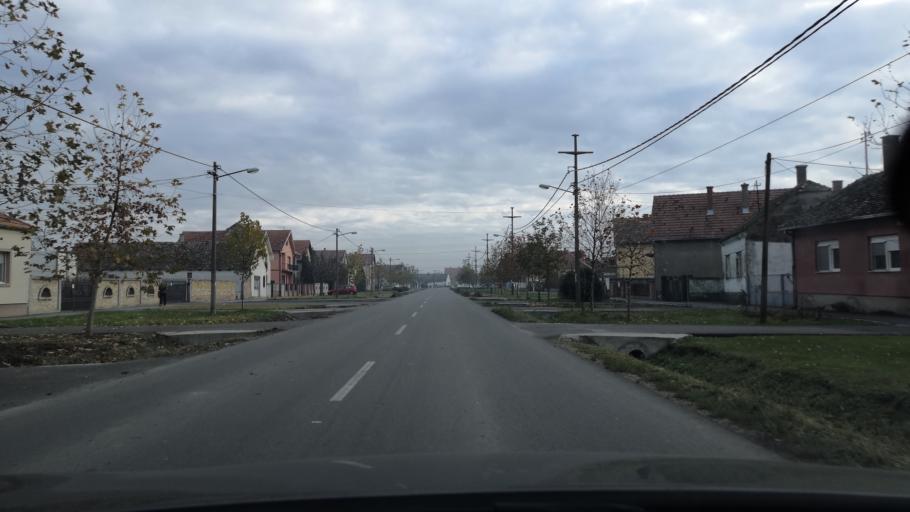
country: RS
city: Ugrinovci
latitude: 44.8788
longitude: 20.1761
